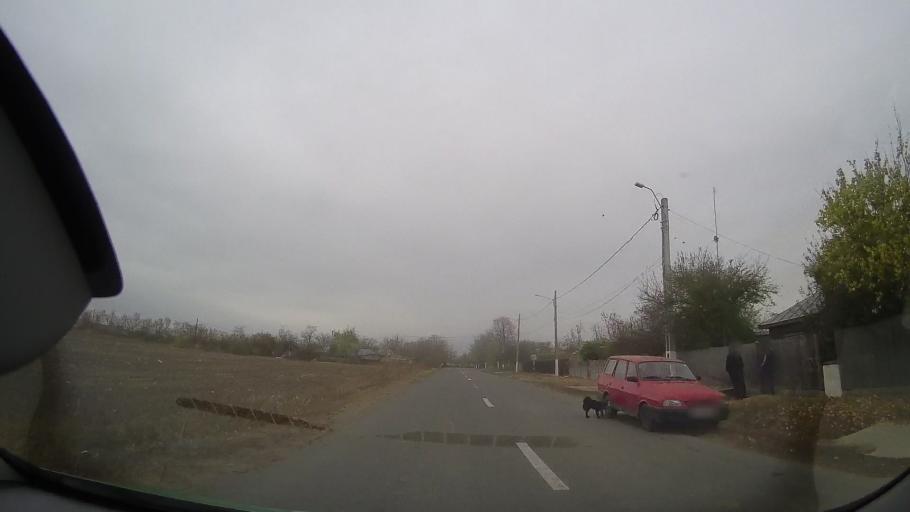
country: RO
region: Braila
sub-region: Comuna Budesti
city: Tataru
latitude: 44.8421
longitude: 27.4260
